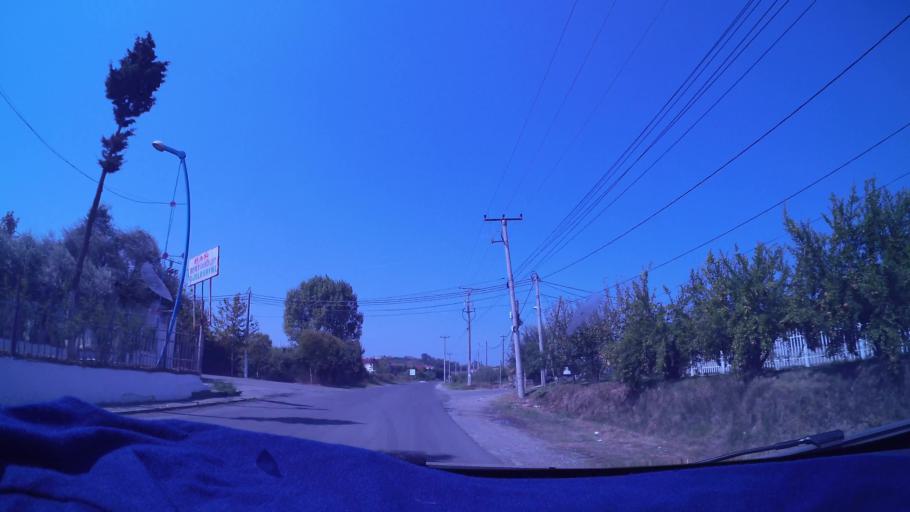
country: AL
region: Durres
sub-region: Rrethi i Durresit
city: Shijak
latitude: 41.3648
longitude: 19.5779
